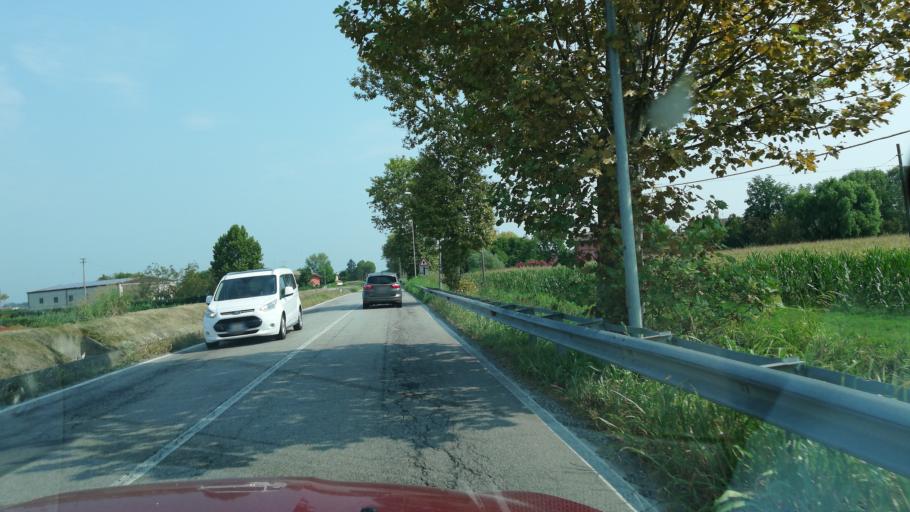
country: IT
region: Veneto
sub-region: Provincia di Venezia
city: Lugugnana
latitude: 45.7416
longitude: 12.9756
